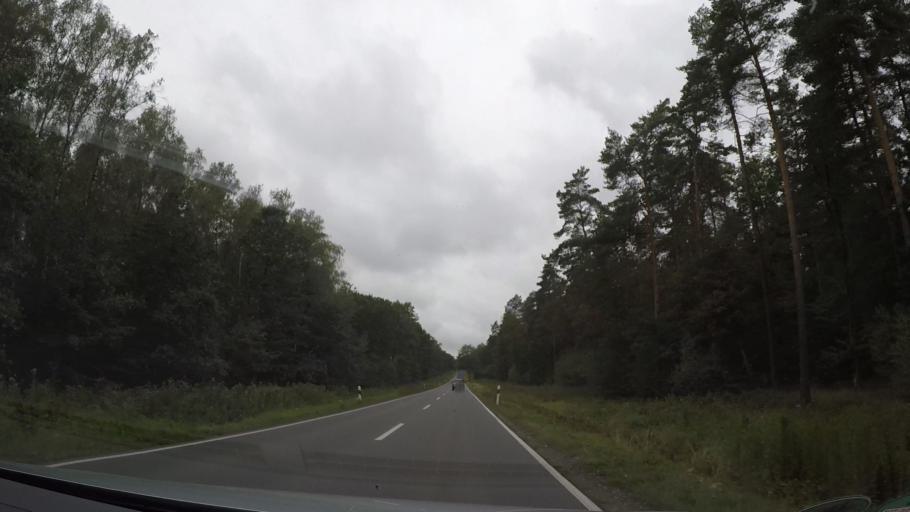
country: DE
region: Saxony-Anhalt
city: Beendorf
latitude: 52.2198
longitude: 11.0712
